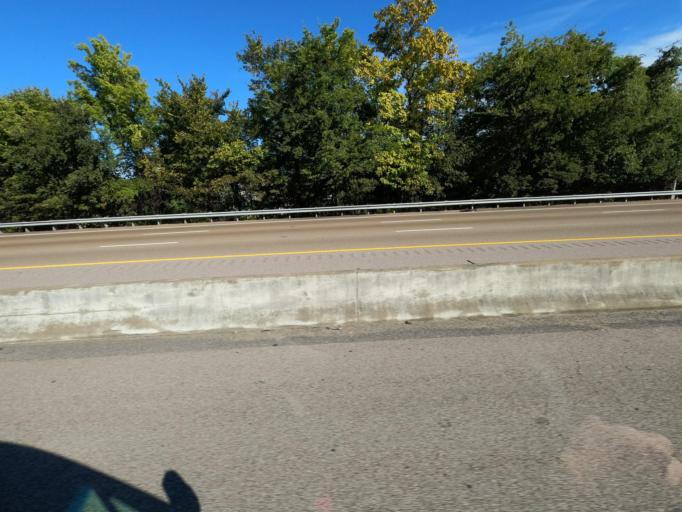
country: US
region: Tennessee
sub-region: Shelby County
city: Memphis
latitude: 35.1219
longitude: -90.0257
